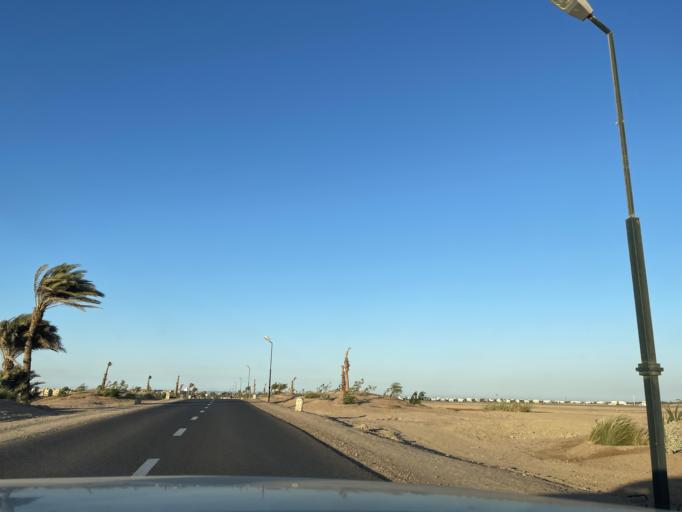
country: EG
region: Red Sea
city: El Gouna
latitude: 27.3734
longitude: 33.6518
